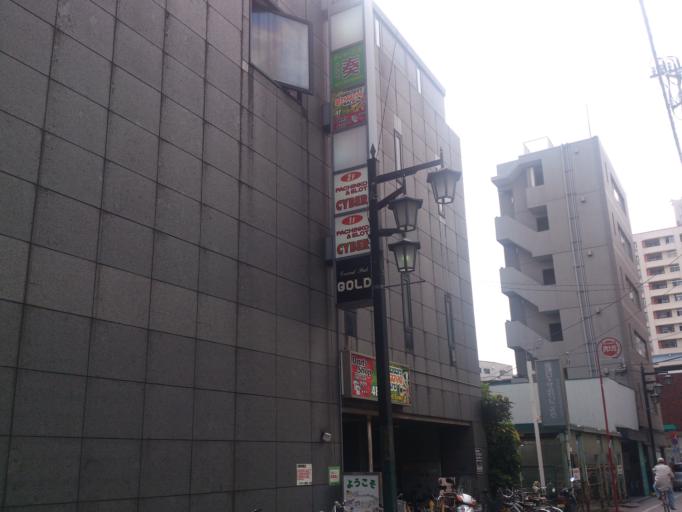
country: JP
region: Chiba
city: Matsudo
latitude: 35.7707
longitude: 139.8714
